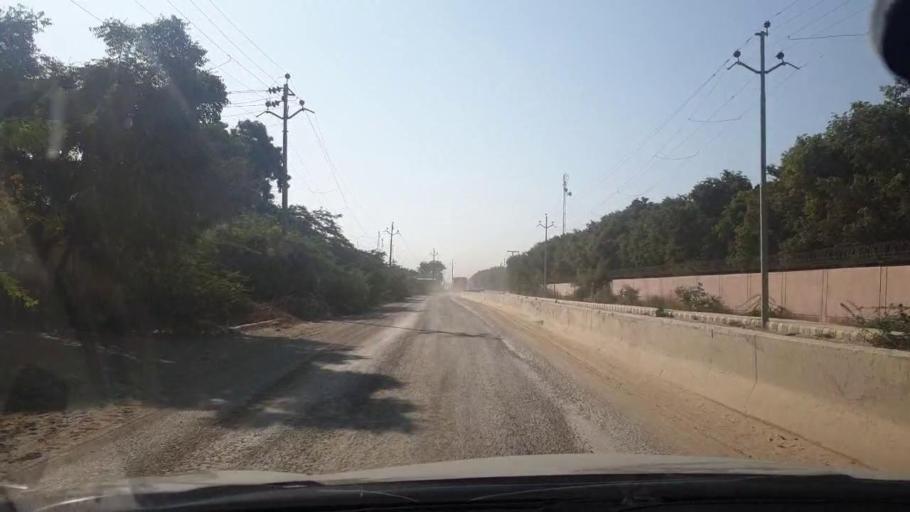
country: PK
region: Sindh
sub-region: Karachi District
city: Karachi
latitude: 25.0861
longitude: 67.0124
